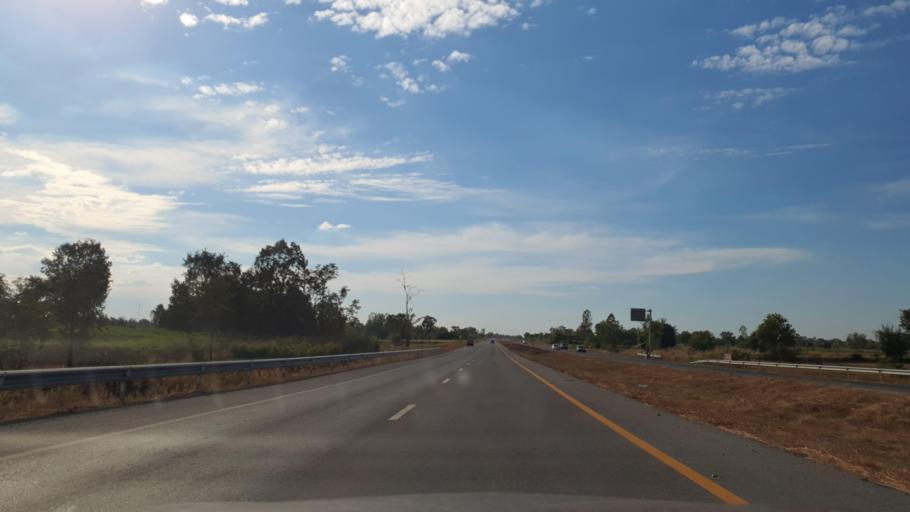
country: TH
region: Kalasin
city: Don Chan
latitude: 16.4116
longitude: 103.7559
